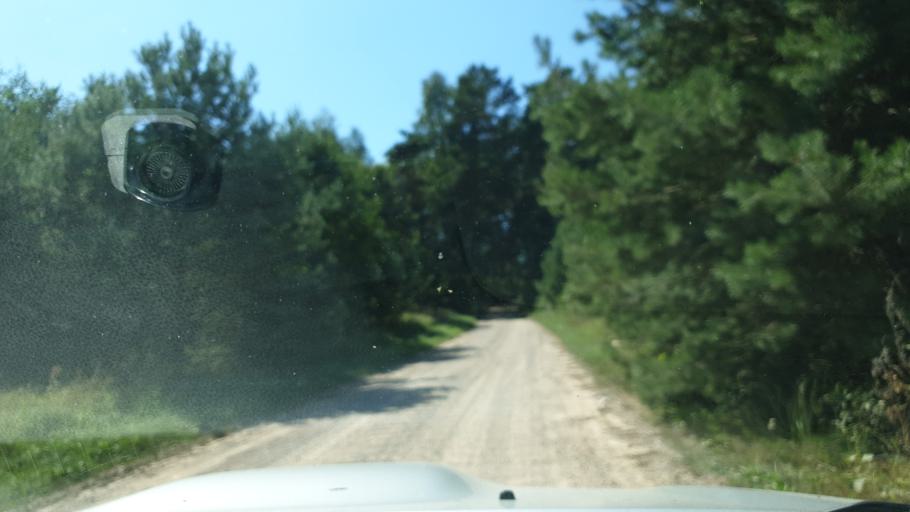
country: LT
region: Vilnius County
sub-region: Vilniaus Rajonas
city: Vievis
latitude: 54.8996
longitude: 24.8755
